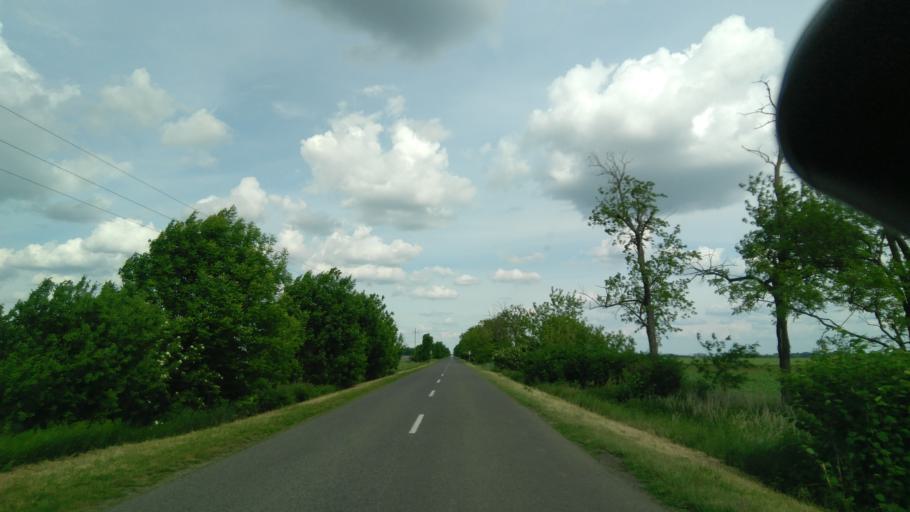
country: RO
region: Arad
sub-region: Comuna Peregu Mare
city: Peregu Mic
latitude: 46.2964
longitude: 20.9599
